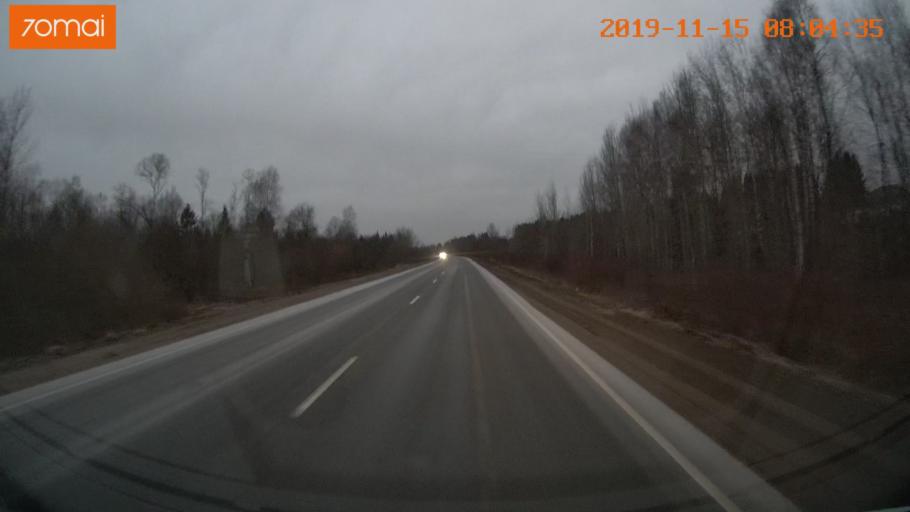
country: RU
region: Vologda
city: Cherepovets
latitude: 59.0097
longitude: 38.0736
